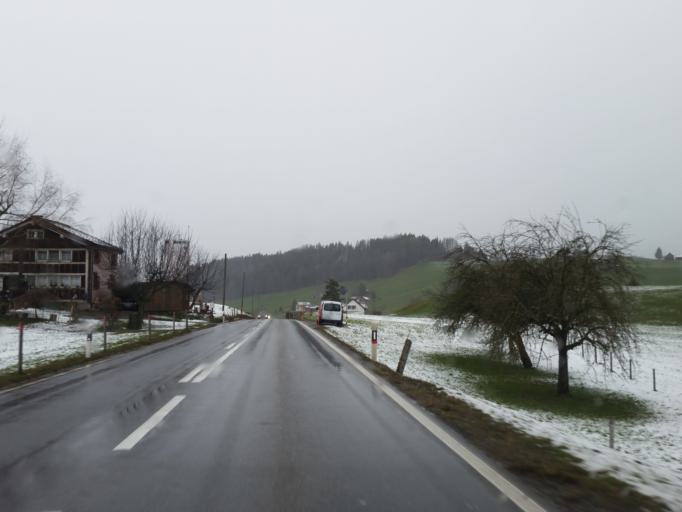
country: CH
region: Appenzell Innerrhoden
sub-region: Appenzell Inner Rhodes
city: Gonten
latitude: 47.3589
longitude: 9.3472
